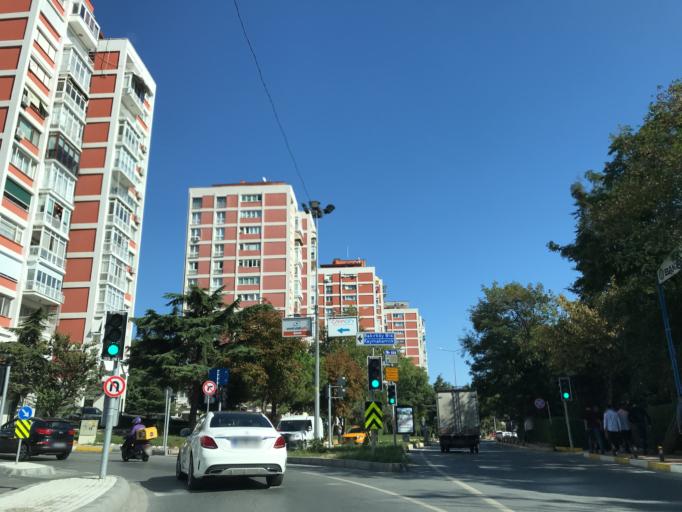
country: TR
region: Istanbul
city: Bahcelievler
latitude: 40.9771
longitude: 28.8685
